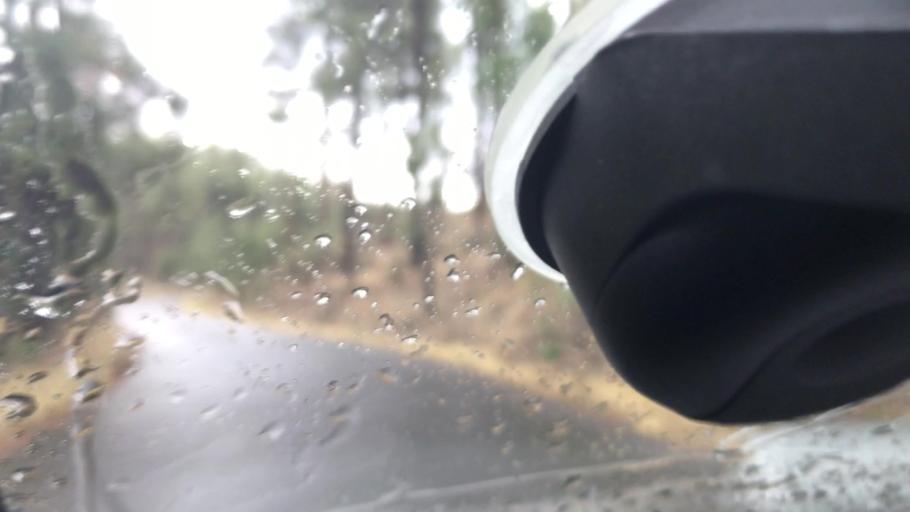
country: US
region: Arizona
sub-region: Yavapai County
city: Prescott
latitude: 34.5103
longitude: -112.3797
